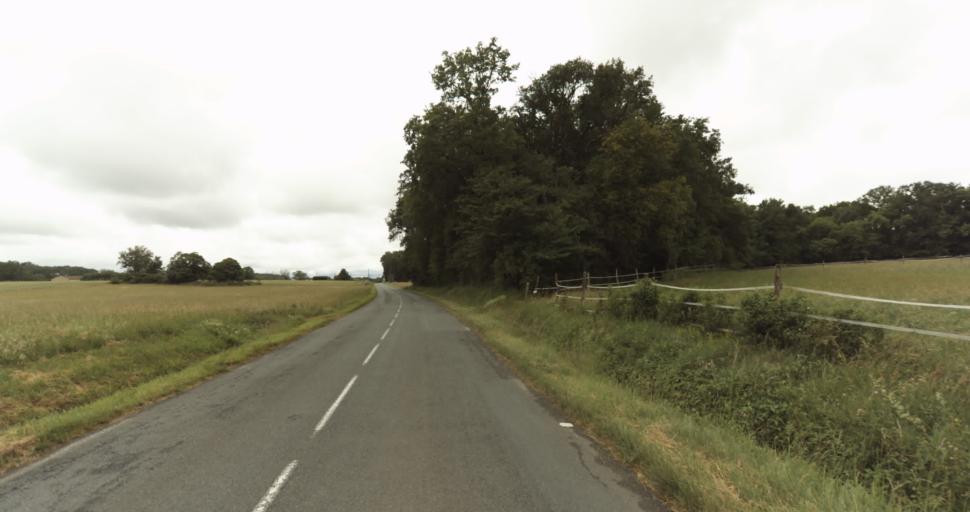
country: FR
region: Aquitaine
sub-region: Departement de la Dordogne
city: Beaumont-du-Perigord
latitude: 44.6923
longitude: 0.8747
